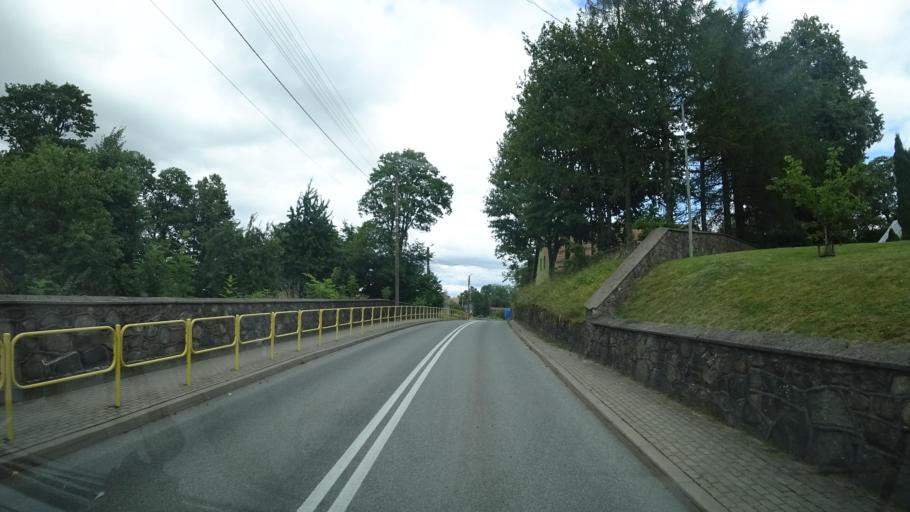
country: PL
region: Warmian-Masurian Voivodeship
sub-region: Powiat goldapski
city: Goldap
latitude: 54.2261
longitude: 22.2411
